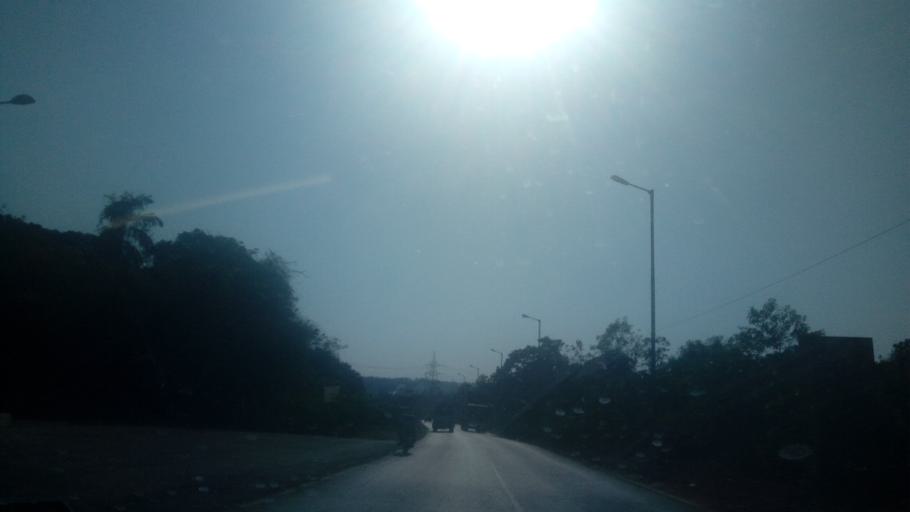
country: IN
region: Goa
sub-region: North Goa
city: Navelim
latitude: 15.5291
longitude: 73.9829
